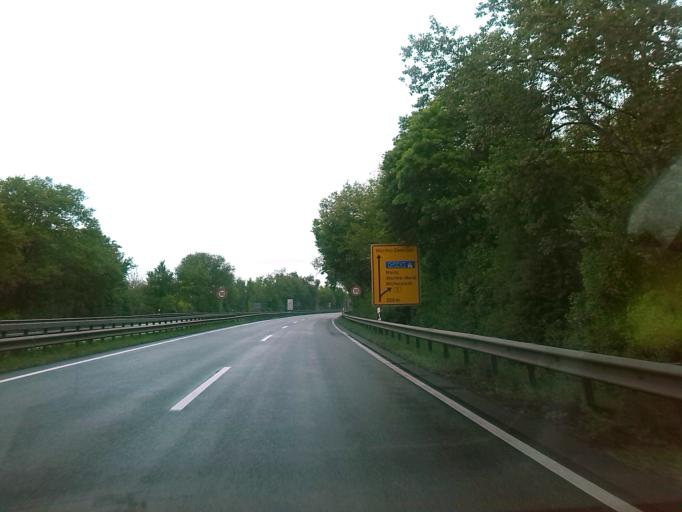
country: DE
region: Rheinland-Pfalz
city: Worms
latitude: 49.6154
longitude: 8.3692
